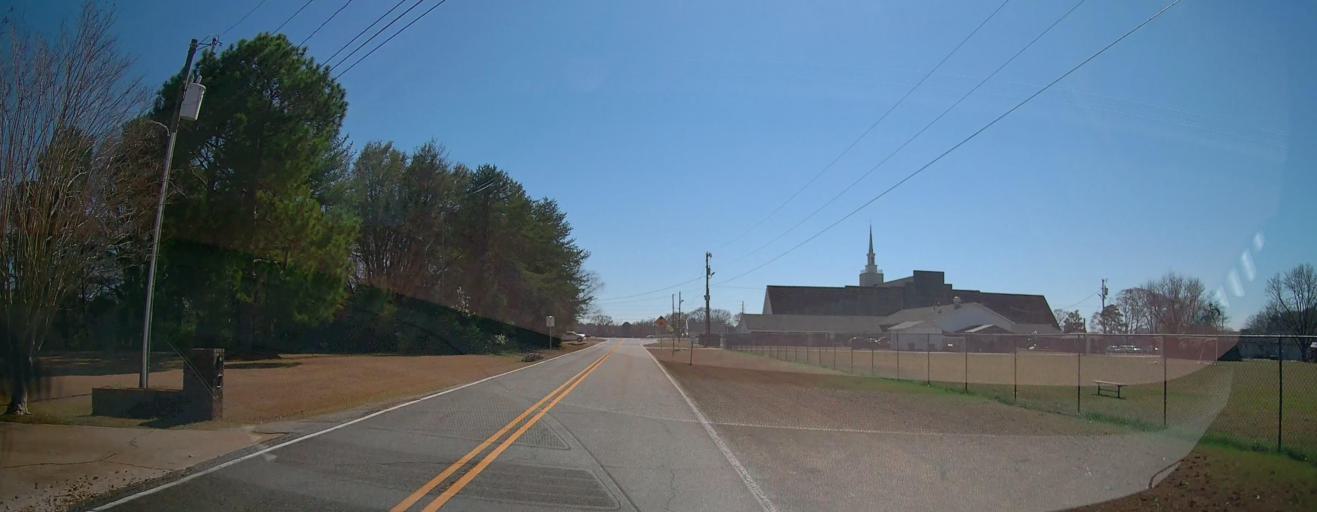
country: US
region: Georgia
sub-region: Houston County
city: Robins Air Force Base
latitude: 32.5564
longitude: -83.6367
